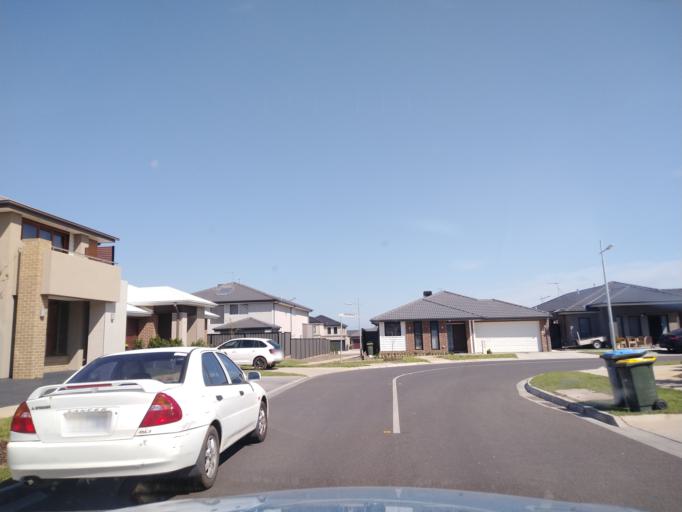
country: AU
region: Victoria
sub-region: Wyndham
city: Williams Landing
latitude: -37.8404
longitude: 144.7431
